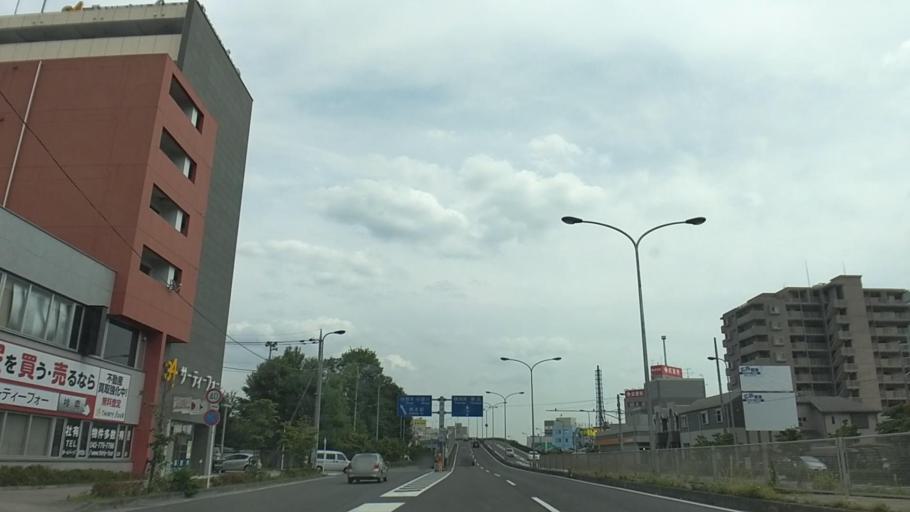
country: JP
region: Tokyo
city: Hachioji
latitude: 35.5886
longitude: 139.3430
